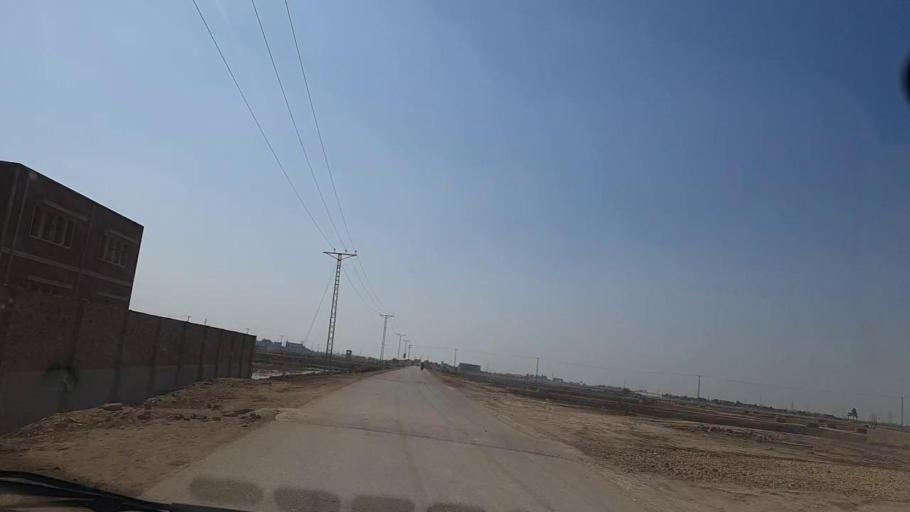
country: PK
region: Sindh
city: Mirpur Khas
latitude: 25.5178
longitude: 68.9635
